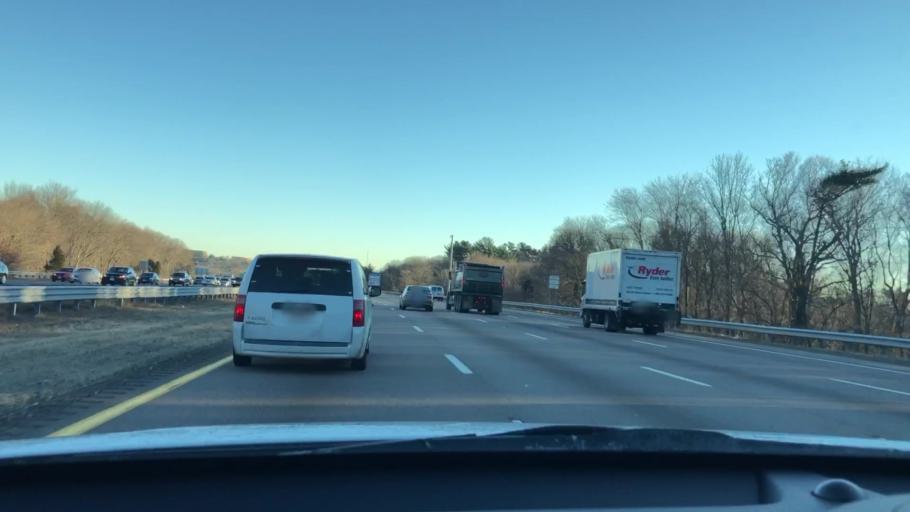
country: US
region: Massachusetts
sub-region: Norfolk County
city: Milton
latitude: 42.2104
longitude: -71.0459
